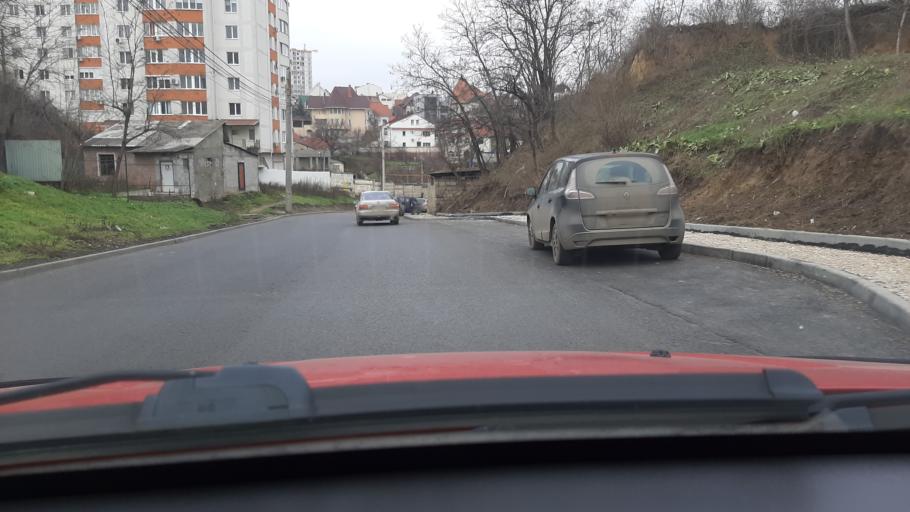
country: MD
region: Chisinau
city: Chisinau
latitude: 47.0045
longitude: 28.8375
